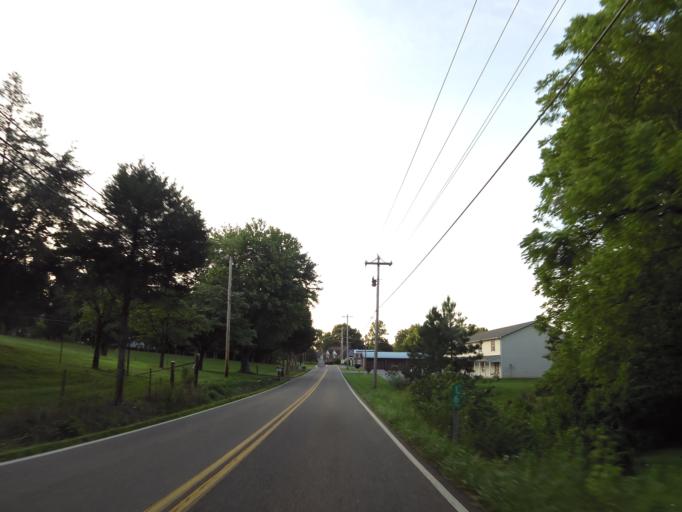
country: US
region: Tennessee
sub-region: Blount County
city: Maryville
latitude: 35.7011
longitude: -83.9657
